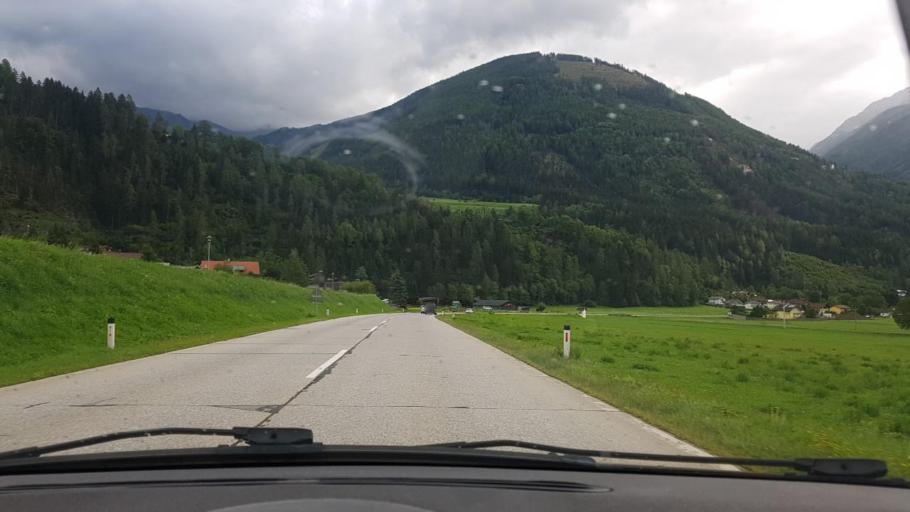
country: AT
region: Carinthia
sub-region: Politischer Bezirk Spittal an der Drau
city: Obervellach
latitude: 46.9368
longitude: 13.1725
